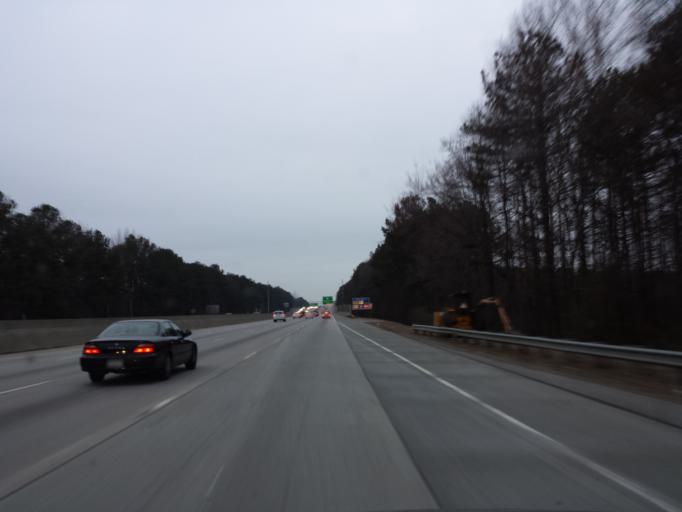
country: US
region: Georgia
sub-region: Fulton County
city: Roswell
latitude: 34.0332
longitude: -84.3162
